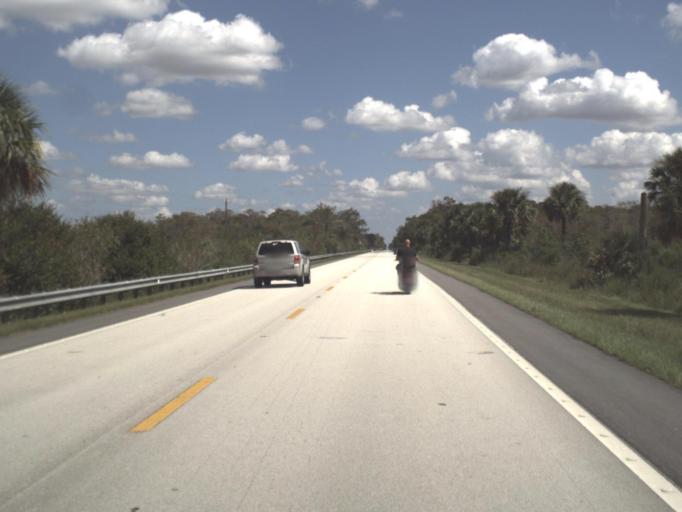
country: US
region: Florida
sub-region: Collier County
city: Marco
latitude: 25.8729
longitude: -81.1908
